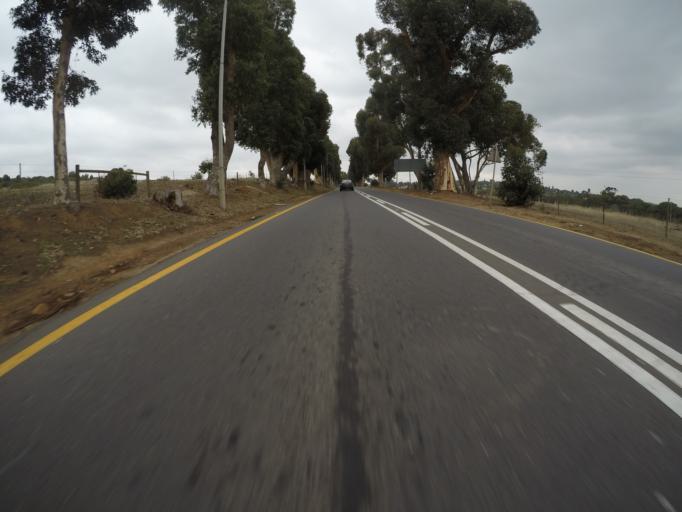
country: ZA
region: Western Cape
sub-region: City of Cape Town
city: Kraaifontein
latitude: -33.8427
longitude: 18.6249
